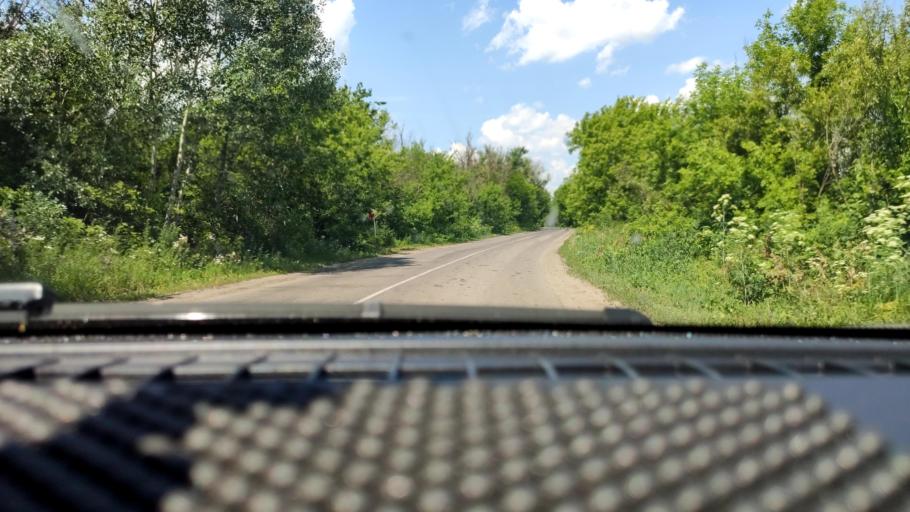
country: RU
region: Voronezj
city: Podkletnoye
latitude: 51.6157
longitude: 39.5709
